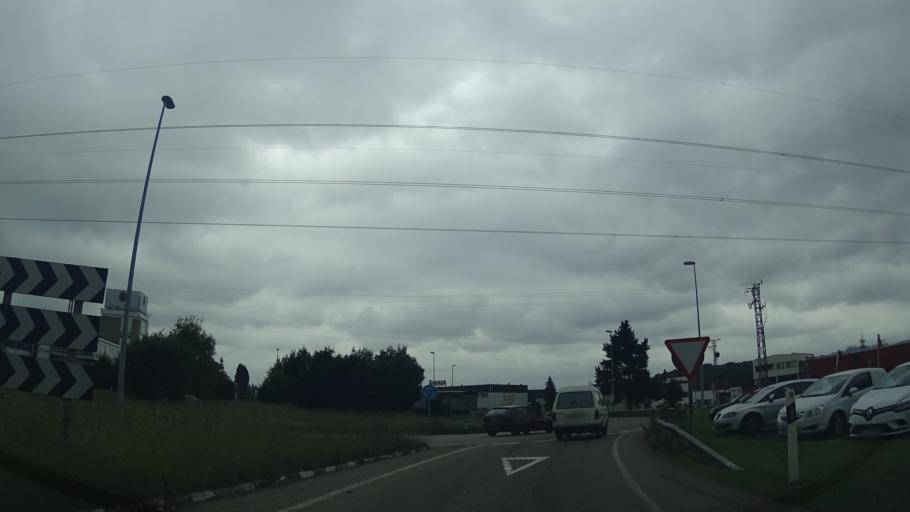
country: ES
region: Asturias
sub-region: Province of Asturias
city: Norena
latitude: 43.3834
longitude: -5.7582
